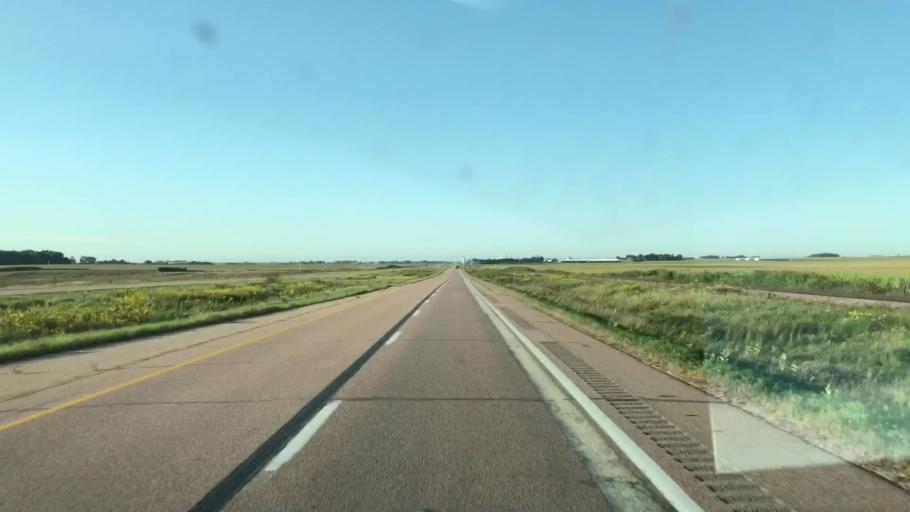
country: US
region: Iowa
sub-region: Osceola County
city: Sibley
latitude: 43.3664
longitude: -95.7652
